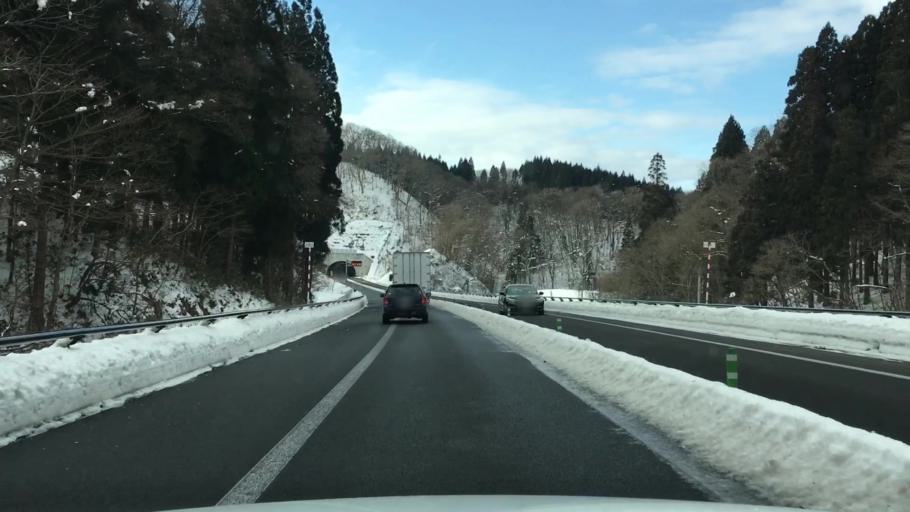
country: JP
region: Akita
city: Takanosu
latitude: 40.2246
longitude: 140.4341
